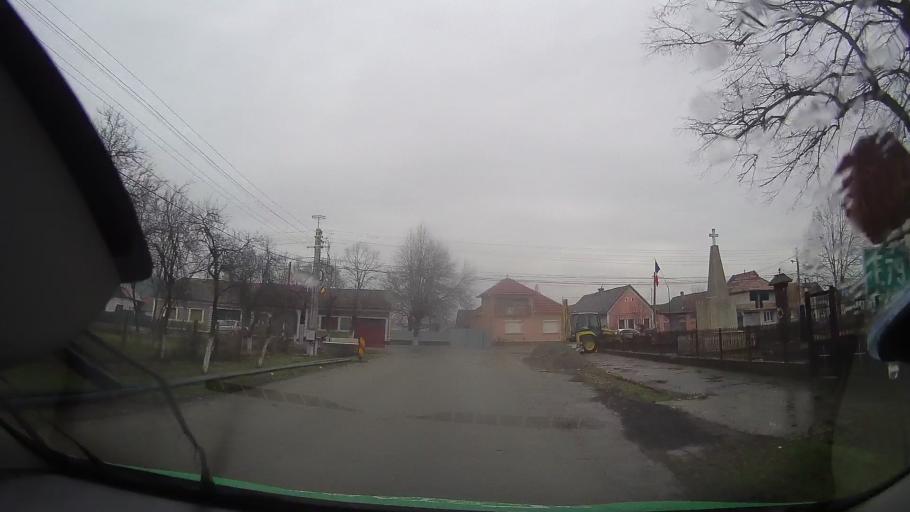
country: RO
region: Bihor
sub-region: Comuna Sambata
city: Sambata
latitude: 46.8012
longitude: 22.2015
